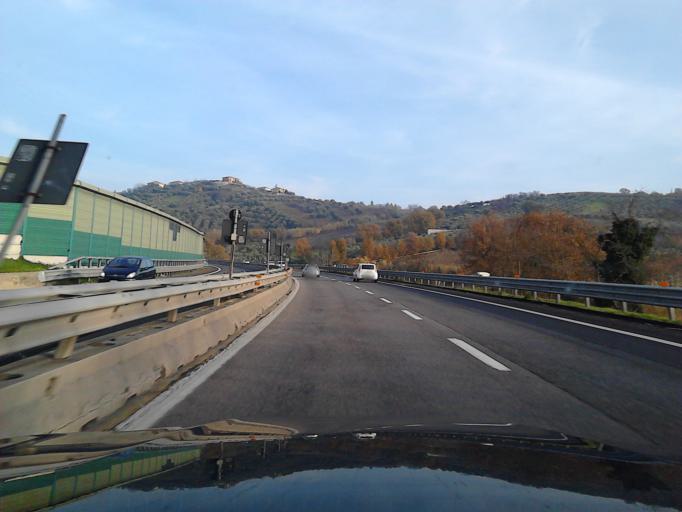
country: IT
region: Abruzzo
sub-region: Provincia di Chieti
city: Sambuceto
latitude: 42.3942
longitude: 14.1763
